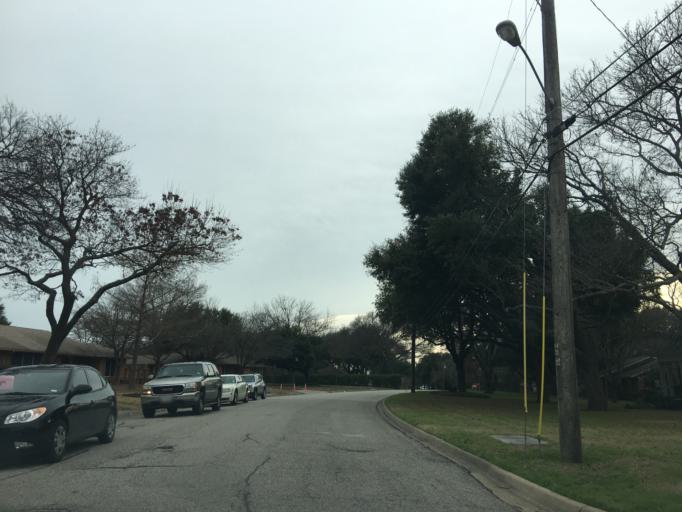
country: US
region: Texas
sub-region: Collin County
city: McKinney
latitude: 33.2017
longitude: -96.6317
